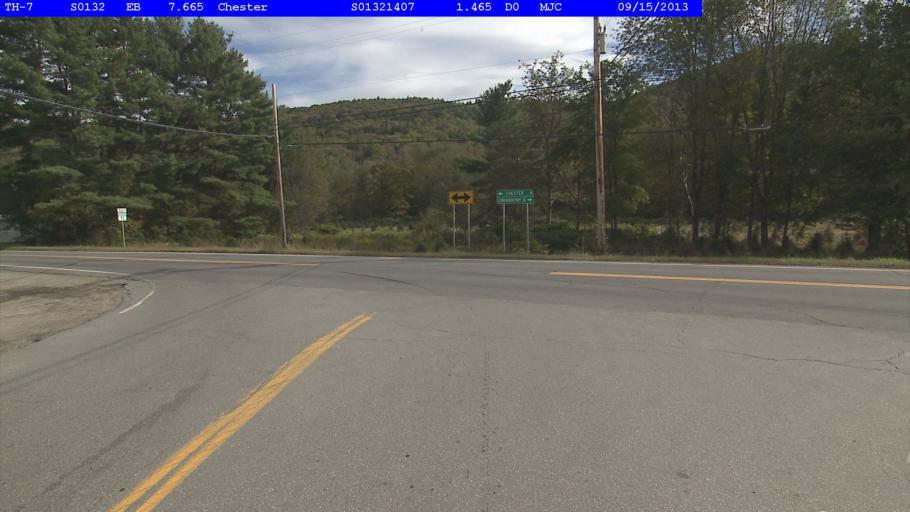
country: US
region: Vermont
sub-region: Windsor County
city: Chester
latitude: 43.2623
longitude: -72.6615
